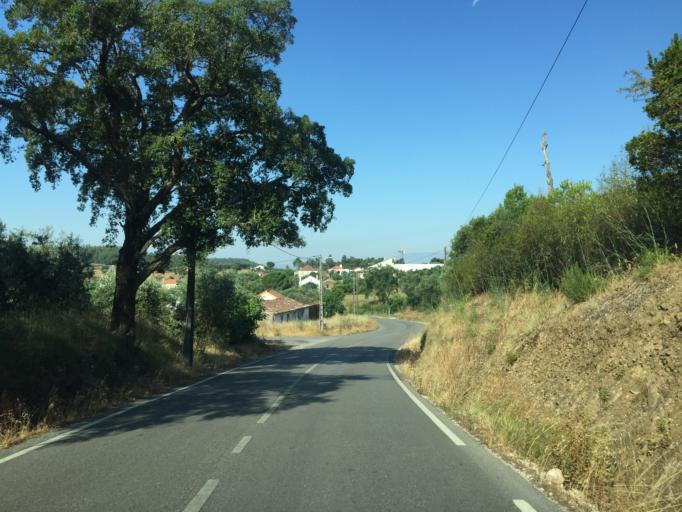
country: PT
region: Santarem
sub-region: Tomar
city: Tomar
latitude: 39.5978
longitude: -8.3178
